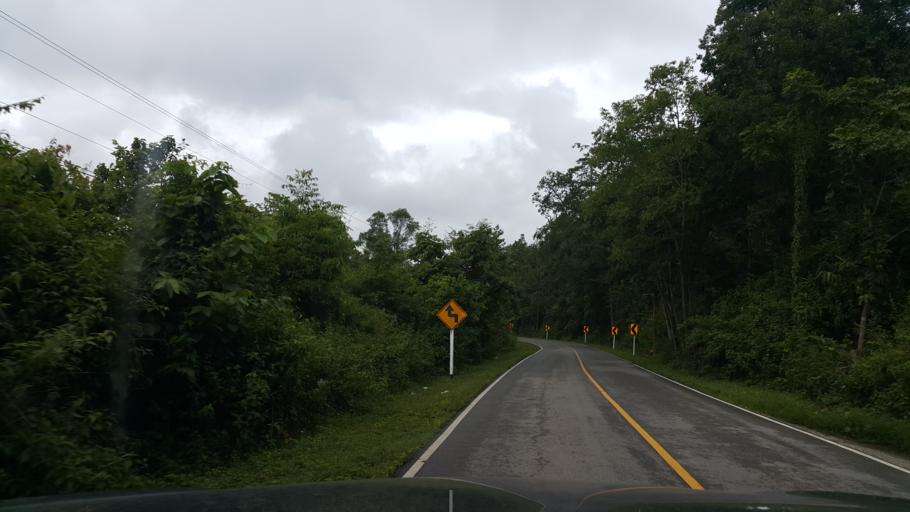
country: TH
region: Chiang Mai
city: Samoeng
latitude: 18.8619
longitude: 98.6648
